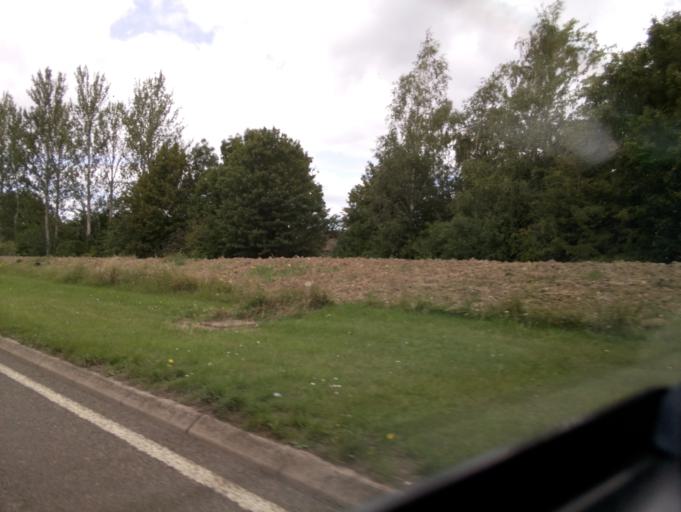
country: GB
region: England
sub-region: Milton Keynes
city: Shenley Church End
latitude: 52.0182
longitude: -0.7882
